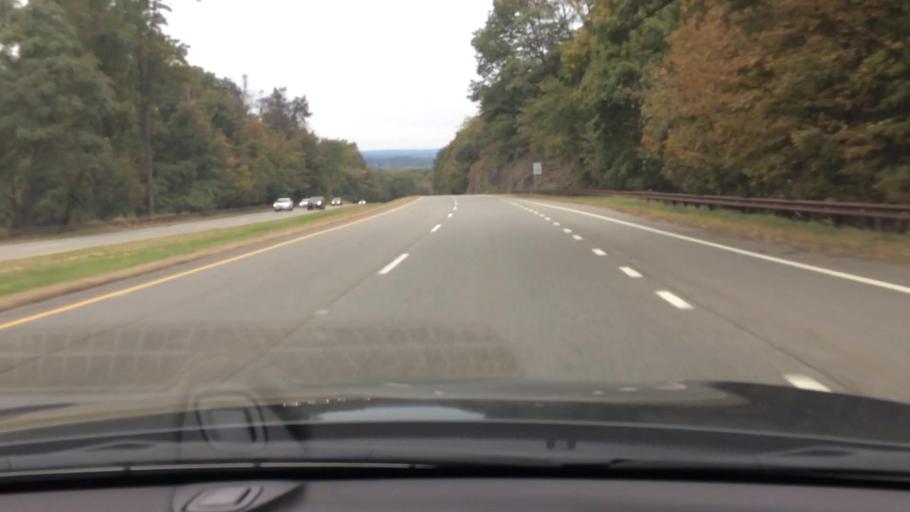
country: US
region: New York
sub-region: Rockland County
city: Sparkill
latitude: 41.0005
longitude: -73.9155
